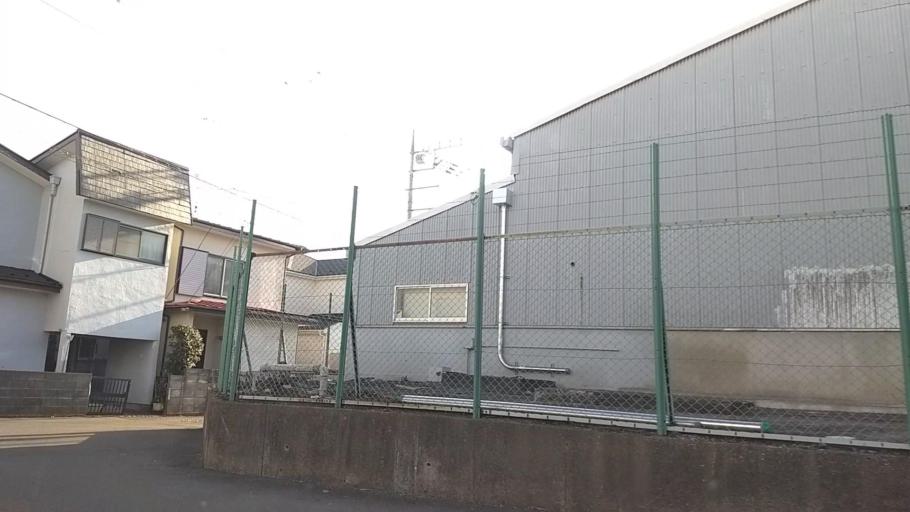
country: JP
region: Kanagawa
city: Atsugi
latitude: 35.4486
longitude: 139.3382
